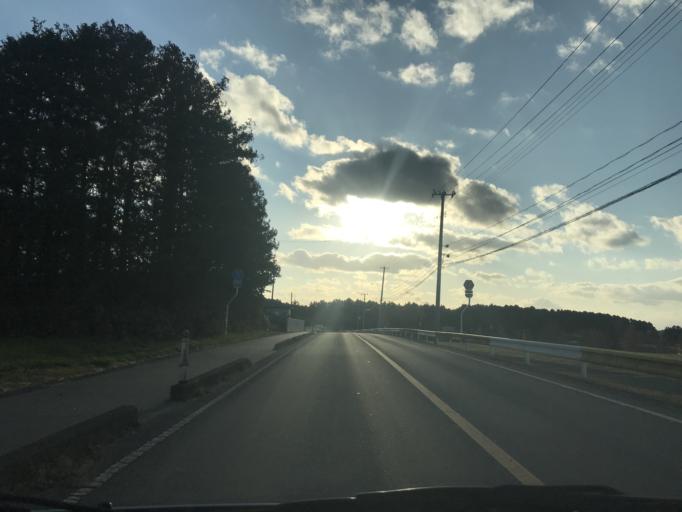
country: JP
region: Miyagi
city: Wakuya
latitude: 38.6880
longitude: 141.1333
